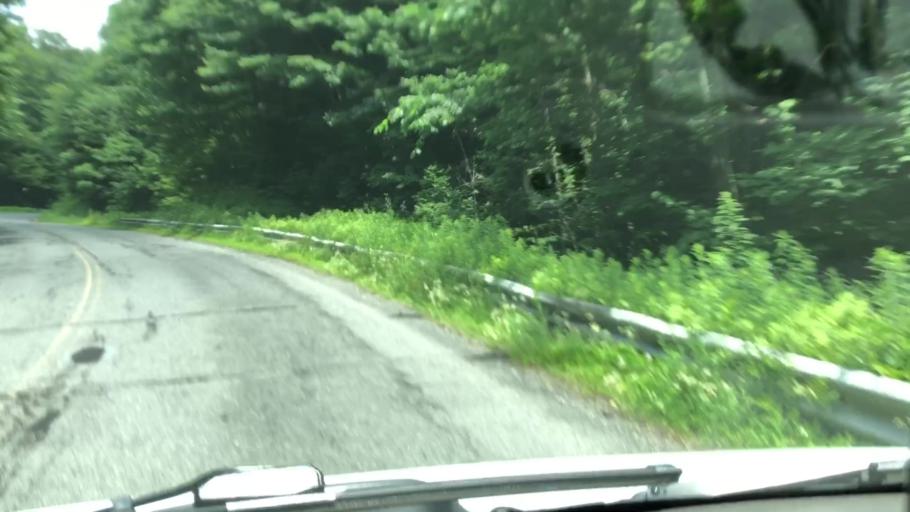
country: US
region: Massachusetts
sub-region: Berkshire County
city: Adams
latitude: 42.5822
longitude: -73.0894
